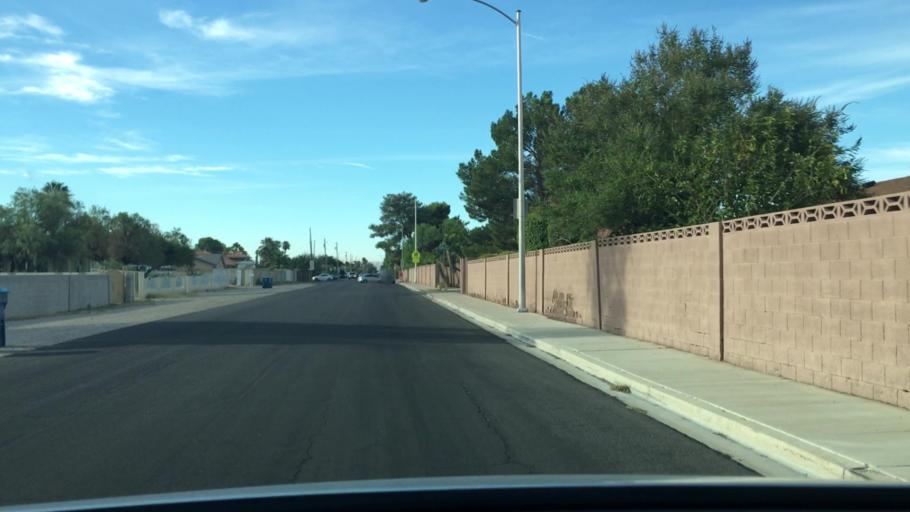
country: US
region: Nevada
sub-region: Clark County
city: Spring Valley
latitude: 36.1325
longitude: -115.2230
